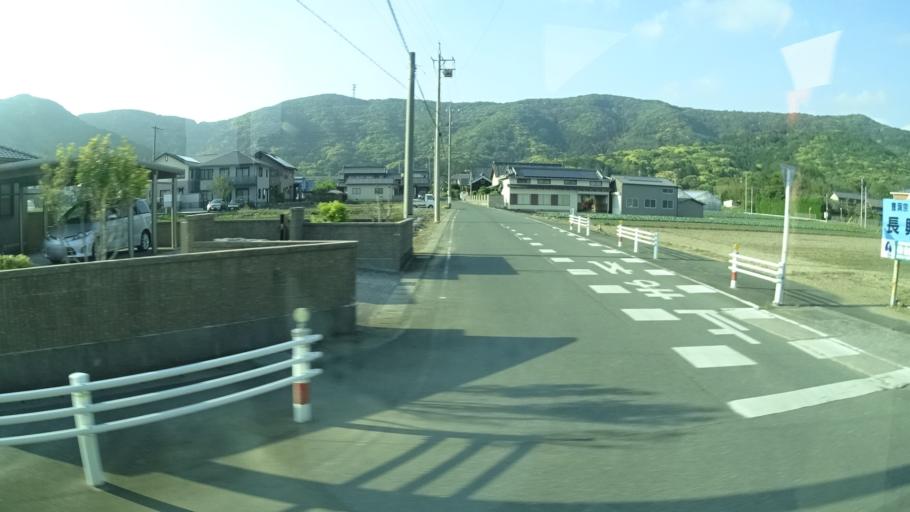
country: JP
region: Aichi
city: Tahara
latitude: 34.6528
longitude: 137.2301
